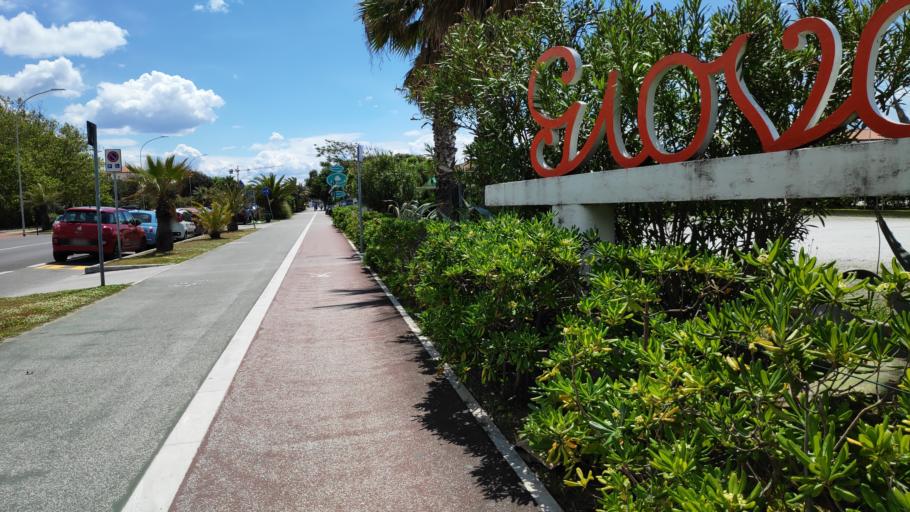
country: IT
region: Tuscany
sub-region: Provincia di Lucca
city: Forte dei Marmi
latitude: 43.9594
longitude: 10.1655
